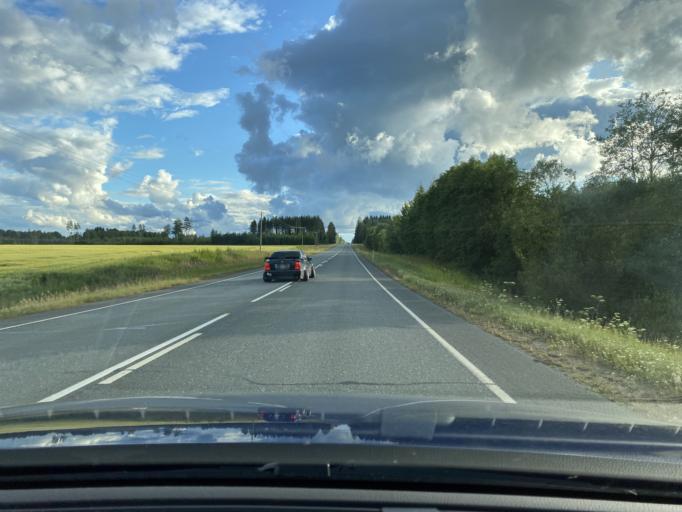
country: FI
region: Haeme
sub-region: Haemeenlinna
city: Renko
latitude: 60.8862
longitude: 24.2493
